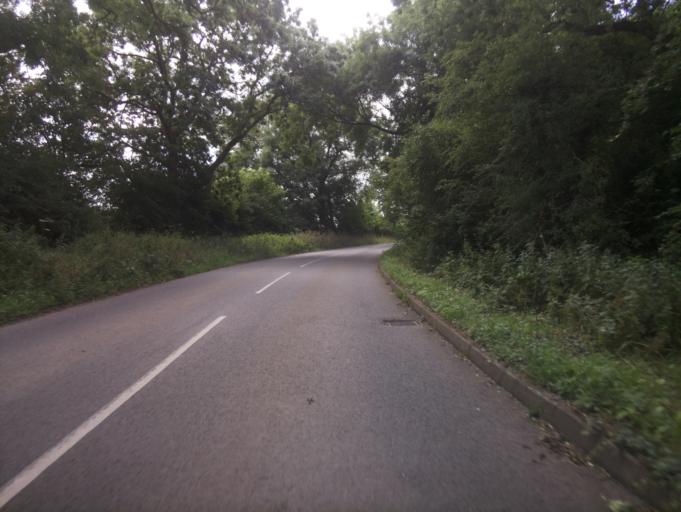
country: GB
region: England
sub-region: Nottinghamshire
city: Ruddington
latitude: 52.8535
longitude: -1.1045
